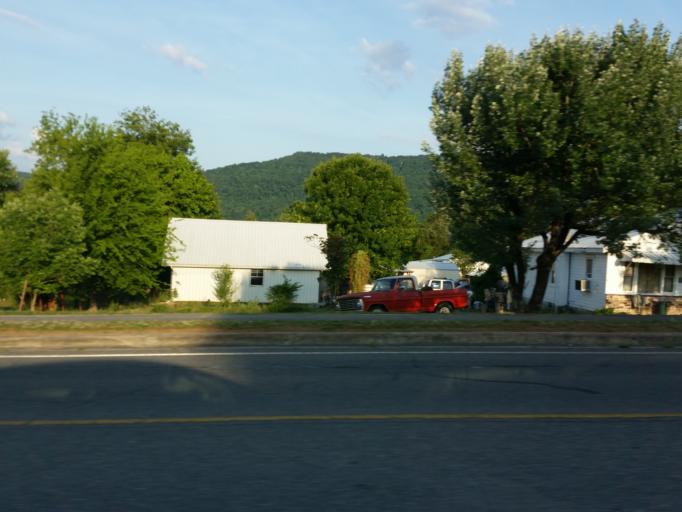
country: US
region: Georgia
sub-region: Dade County
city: Trenton
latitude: 34.8624
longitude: -85.5165
